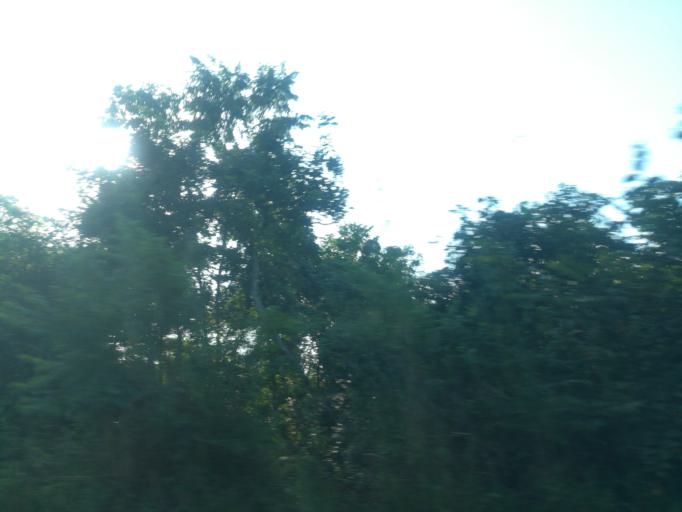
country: NG
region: Ogun
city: Abeokuta
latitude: 7.2561
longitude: 3.3004
